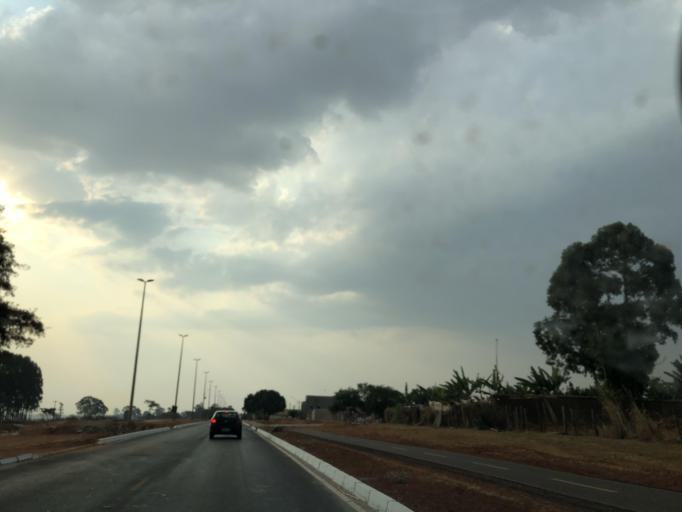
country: BR
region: Federal District
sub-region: Brasilia
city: Brasilia
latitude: -15.9279
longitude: -48.0509
